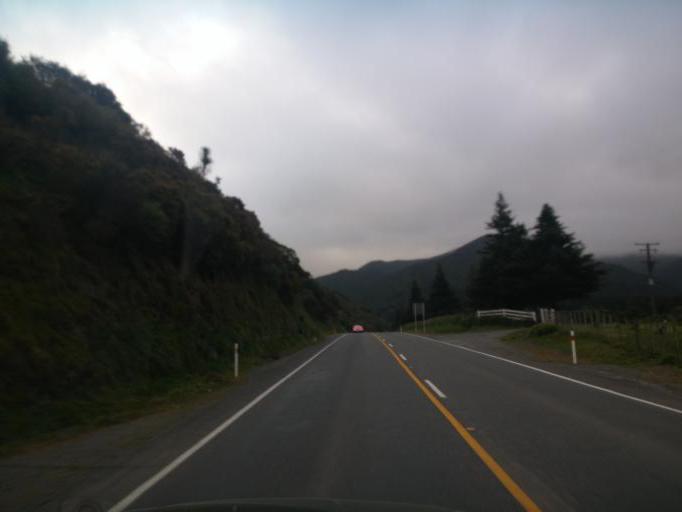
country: NZ
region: Wellington
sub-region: Upper Hutt City
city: Upper Hutt
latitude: -41.1082
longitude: 175.3051
